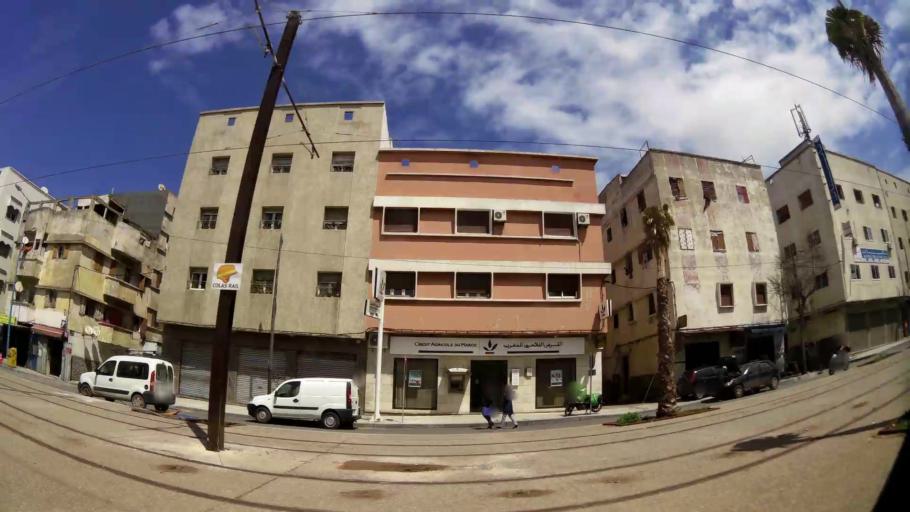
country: MA
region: Grand Casablanca
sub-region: Mediouna
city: Tit Mellil
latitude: 33.6078
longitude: -7.5203
